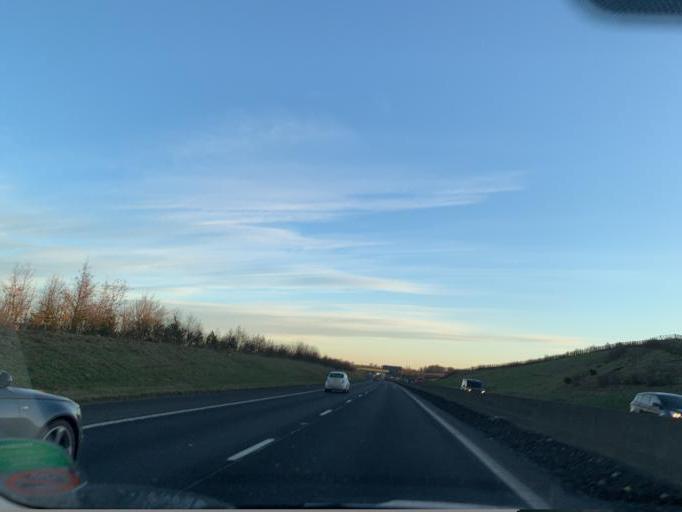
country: GB
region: Scotland
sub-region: North Lanarkshire
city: Chryston
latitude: 55.9114
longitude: -4.1174
